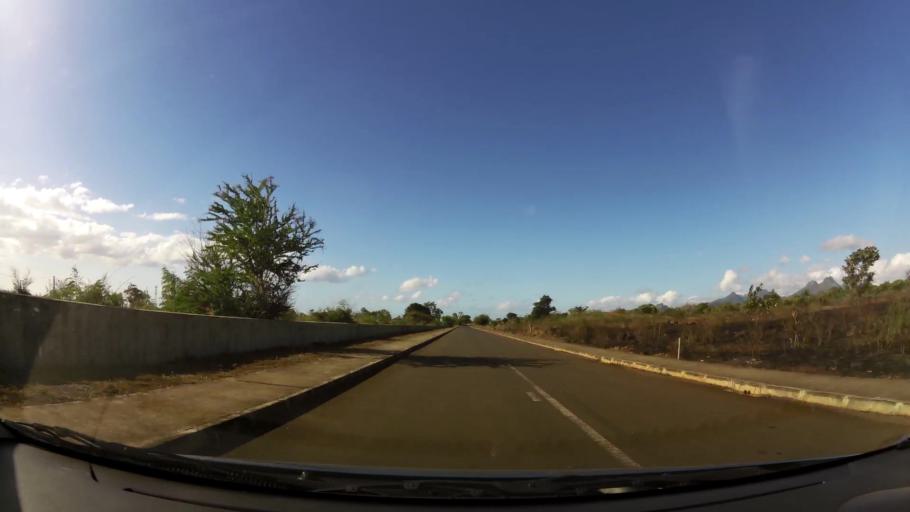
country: MU
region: Black River
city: Albion
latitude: -20.1949
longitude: 57.4105
